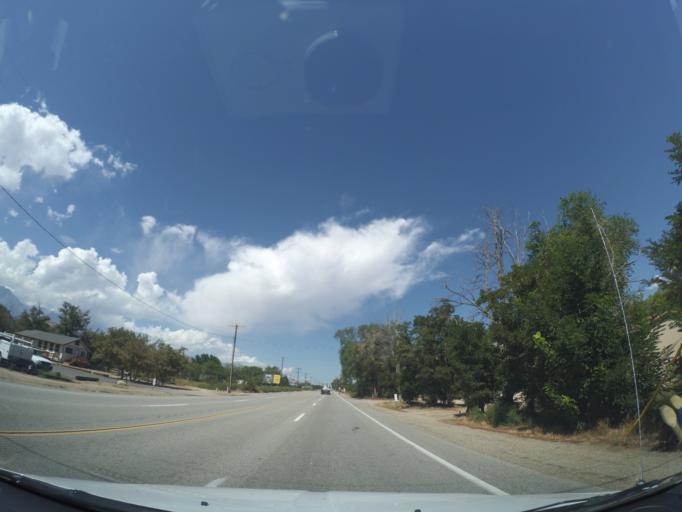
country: US
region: California
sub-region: Inyo County
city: Lone Pine
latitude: 36.5950
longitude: -118.0581
